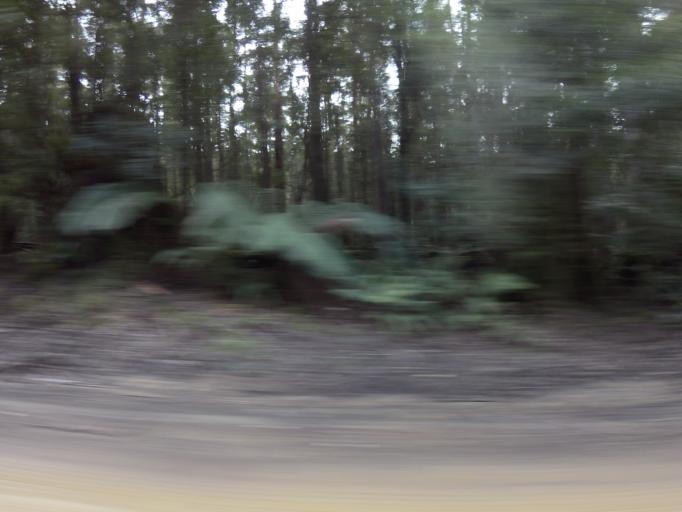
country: AU
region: Tasmania
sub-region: Huon Valley
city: Geeveston
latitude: -43.3861
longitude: 146.8467
